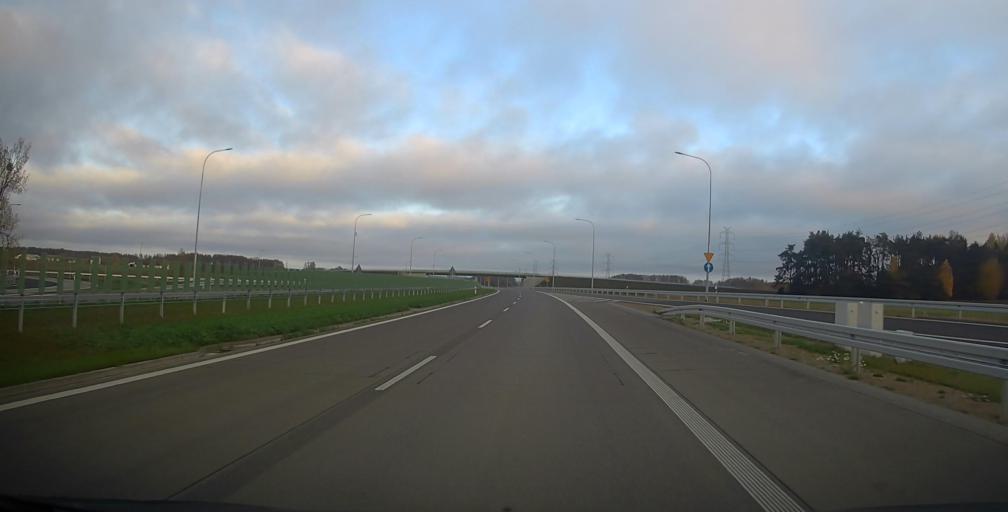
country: PL
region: Podlasie
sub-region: Powiat grajewski
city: Szczuczyn
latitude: 53.5918
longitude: 22.3289
